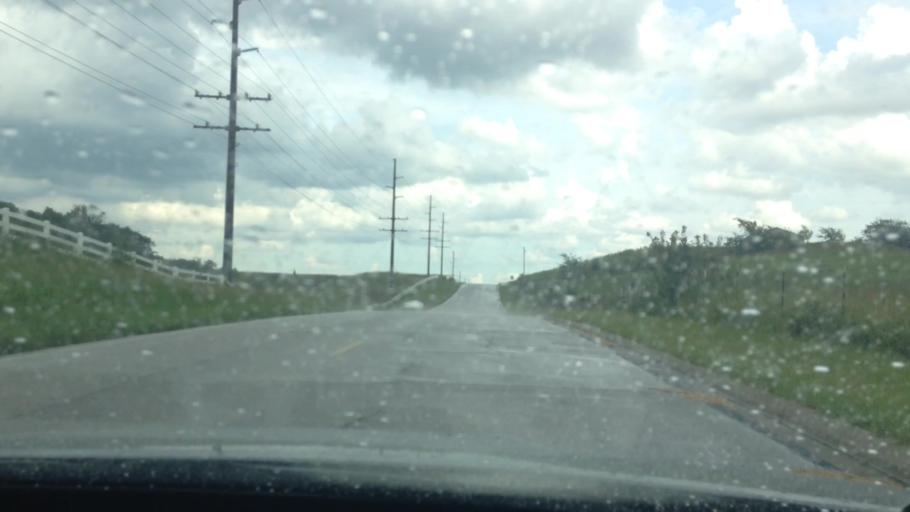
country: US
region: Missouri
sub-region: Platte County
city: Platte City
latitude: 39.3390
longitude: -94.7966
